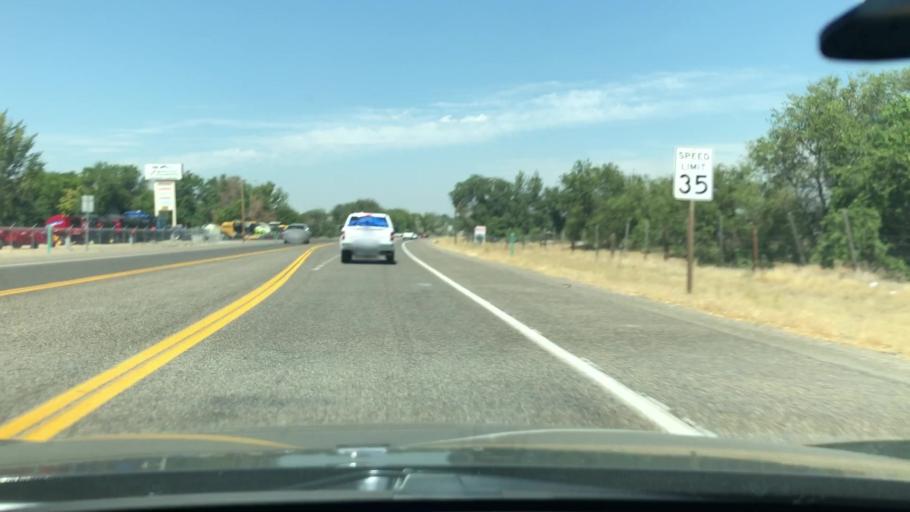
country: US
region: Idaho
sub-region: Owyhee County
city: Homedale
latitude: 43.6088
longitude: -116.9307
